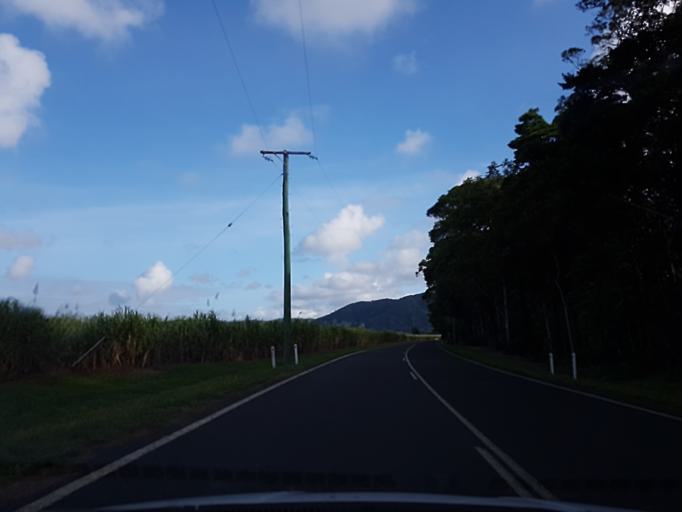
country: AU
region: Queensland
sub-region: Cairns
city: Port Douglas
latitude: -16.2716
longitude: 145.3919
